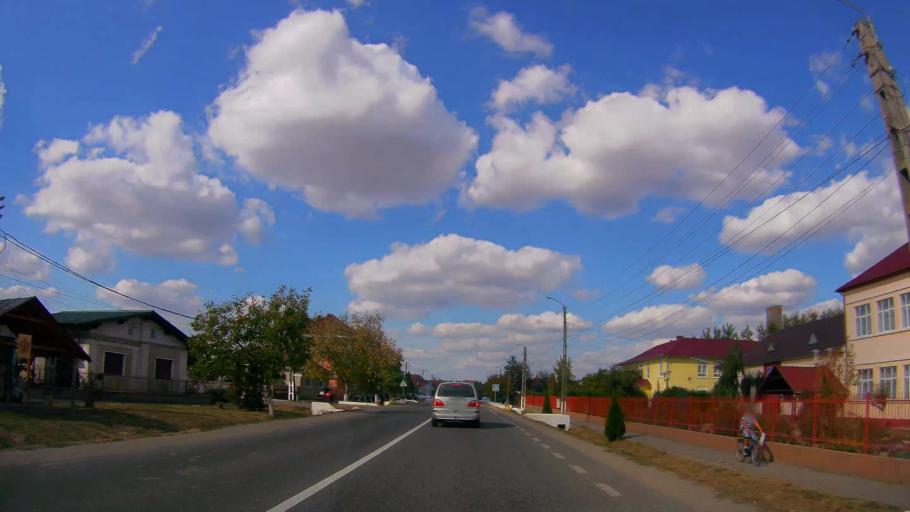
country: RO
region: Satu Mare
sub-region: Oras Ardud
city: Ardud
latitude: 47.6450
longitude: 22.8918
